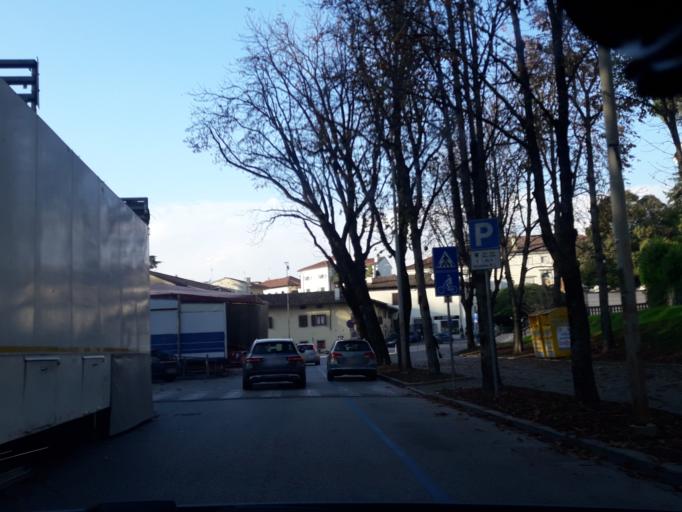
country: IT
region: Friuli Venezia Giulia
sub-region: Provincia di Udine
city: Udine
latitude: 46.0663
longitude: 13.2387
